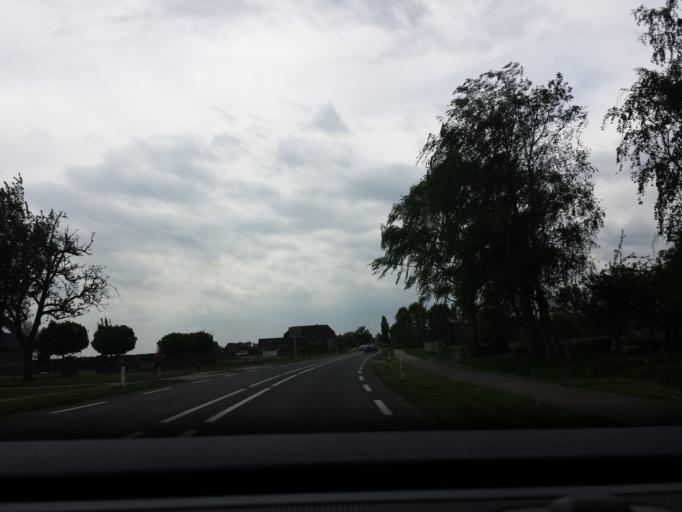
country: NL
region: Gelderland
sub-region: Gemeente Doetinchem
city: Doetinchem
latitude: 51.9310
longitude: 6.2727
